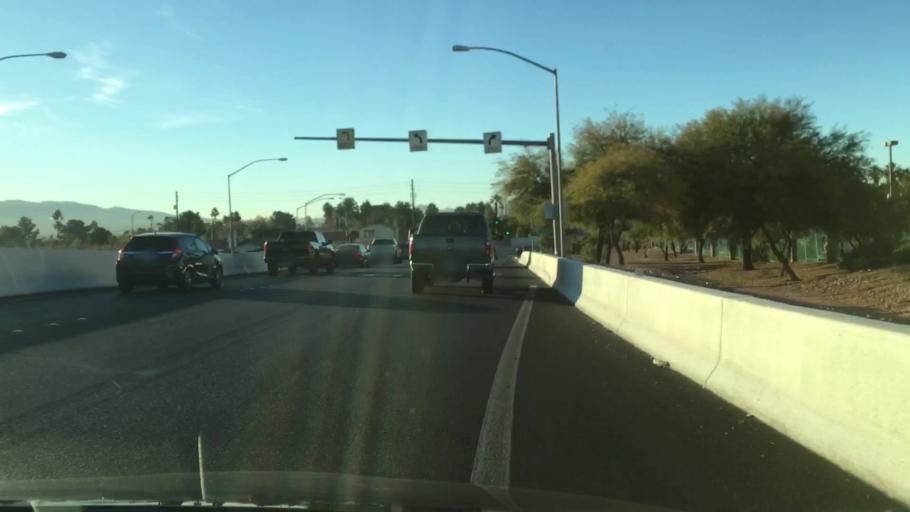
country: US
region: Nevada
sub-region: Clark County
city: Paradise
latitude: 36.0586
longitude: -115.1442
